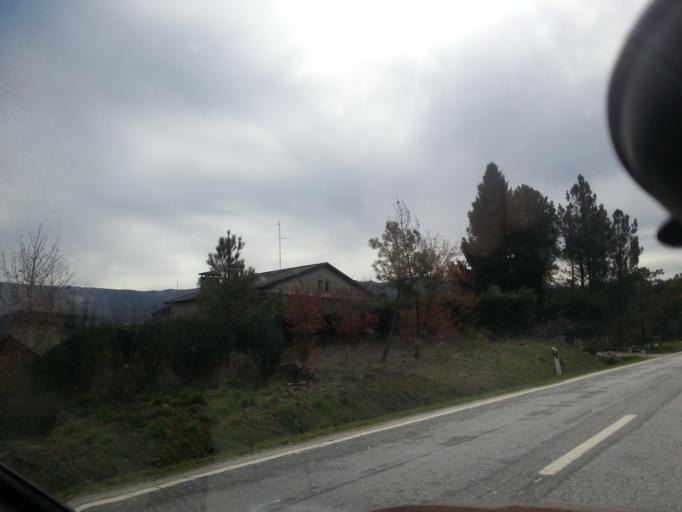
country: PT
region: Guarda
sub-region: Seia
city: Seia
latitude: 40.4460
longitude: -7.7106
